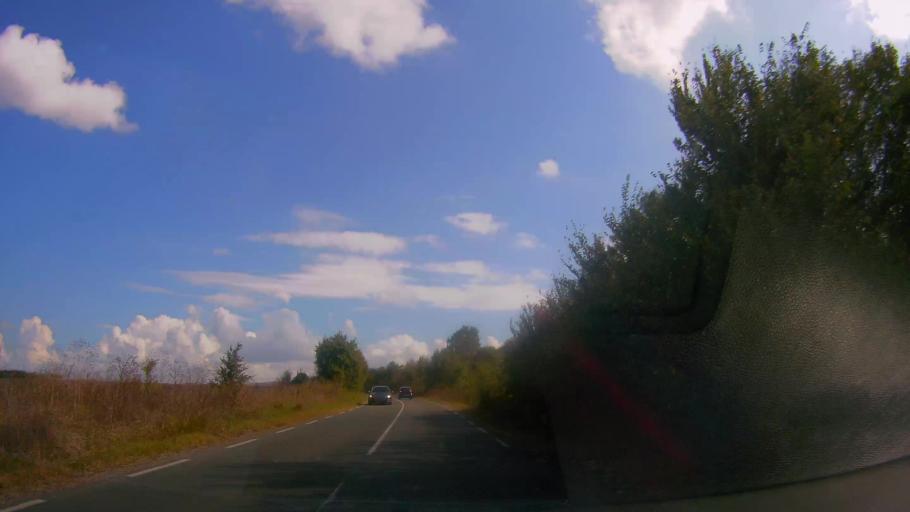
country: BG
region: Burgas
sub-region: Obshtina Kameno
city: Kameno
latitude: 42.4802
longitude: 27.3466
